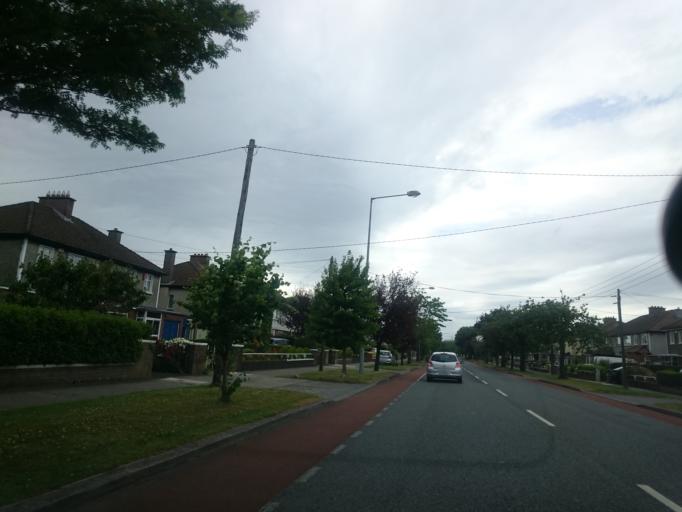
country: IE
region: Leinster
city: Templeogue
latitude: 53.3004
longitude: -6.3021
